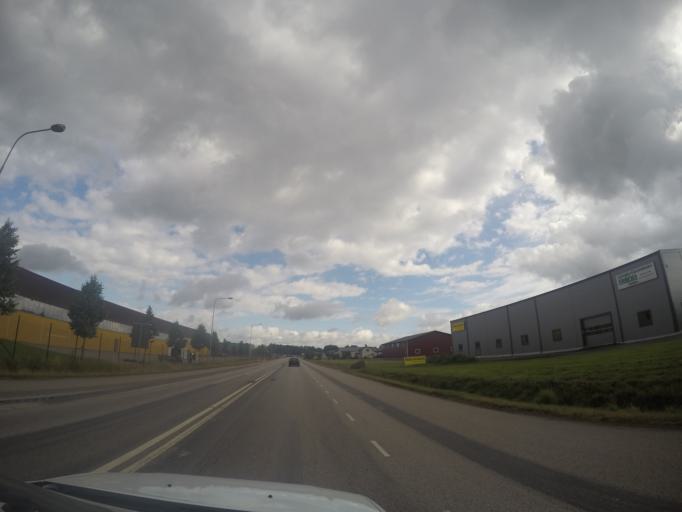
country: SE
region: Kronoberg
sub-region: Ljungby Kommun
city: Ljungby
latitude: 56.8149
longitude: 13.9170
